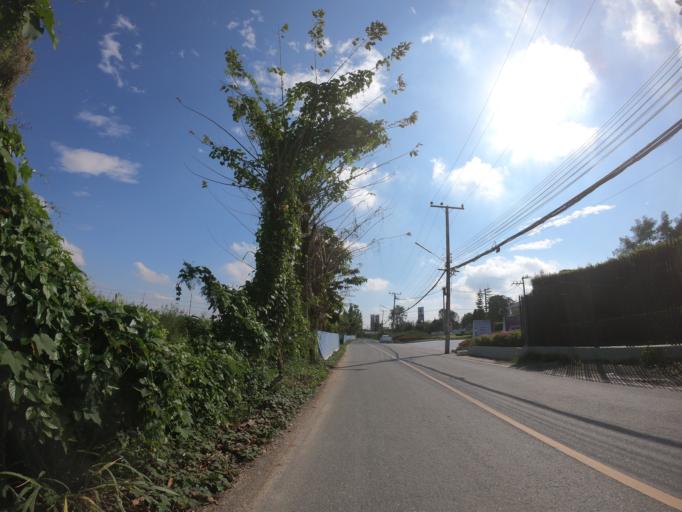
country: TH
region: Chiang Mai
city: San Sai
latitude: 18.8356
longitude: 99.0577
